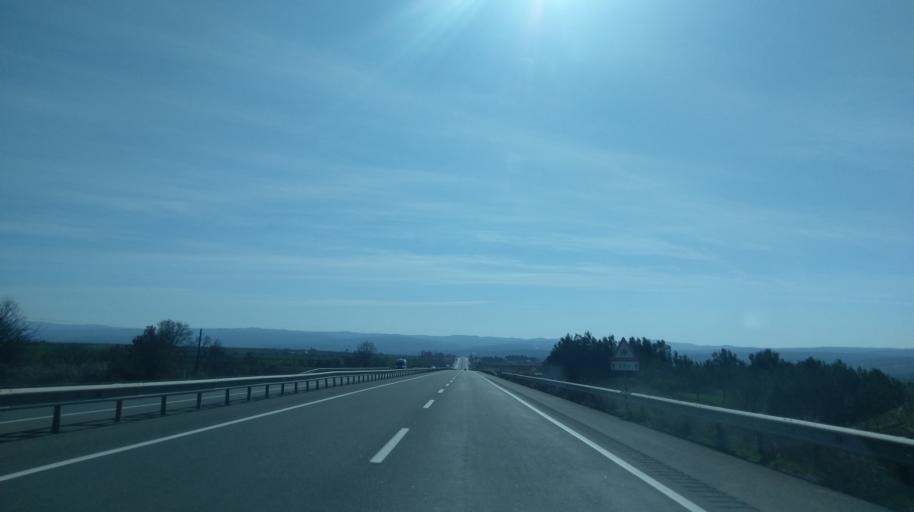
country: TR
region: Edirne
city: Kesan
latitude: 40.7982
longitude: 26.6695
